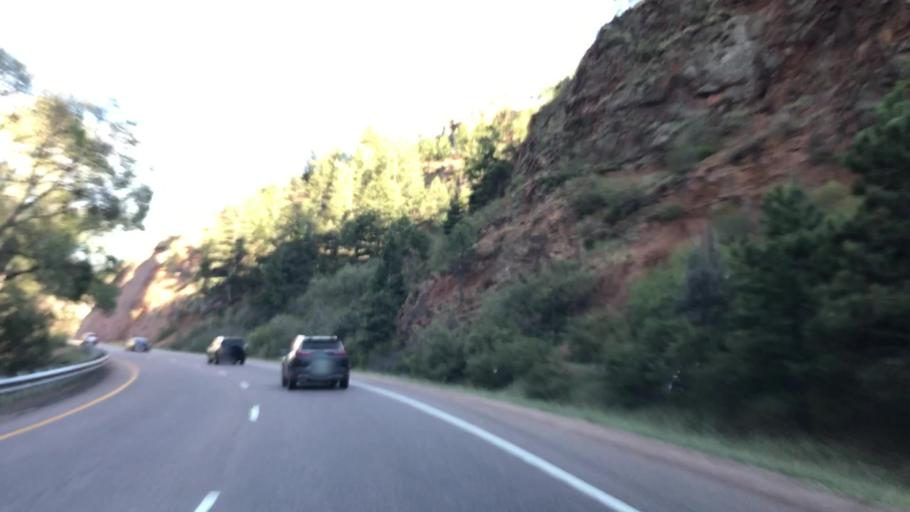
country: US
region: Colorado
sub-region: El Paso County
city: Manitou Springs
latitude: 38.8807
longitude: -104.9497
